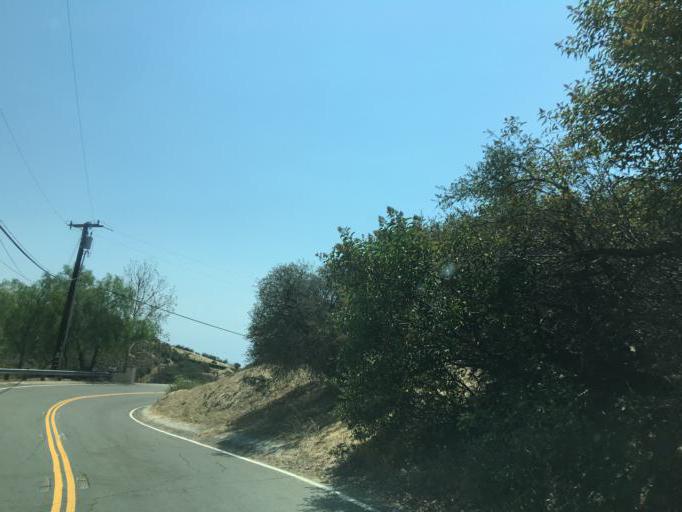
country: US
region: California
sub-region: Los Angeles County
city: Topanga
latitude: 34.0808
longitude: -118.6327
